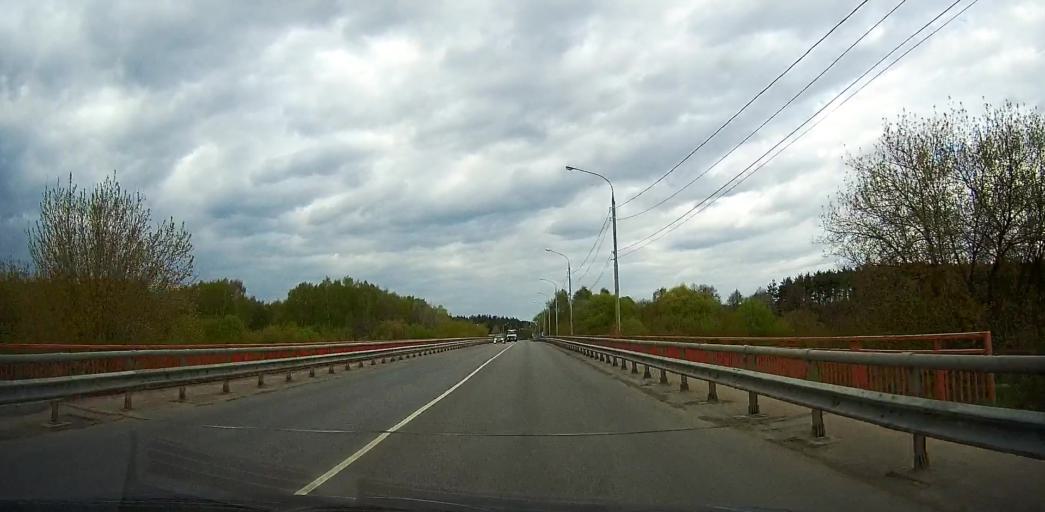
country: RU
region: Moskovskaya
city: Pavlovskiy Posad
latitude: 55.7969
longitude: 38.6529
